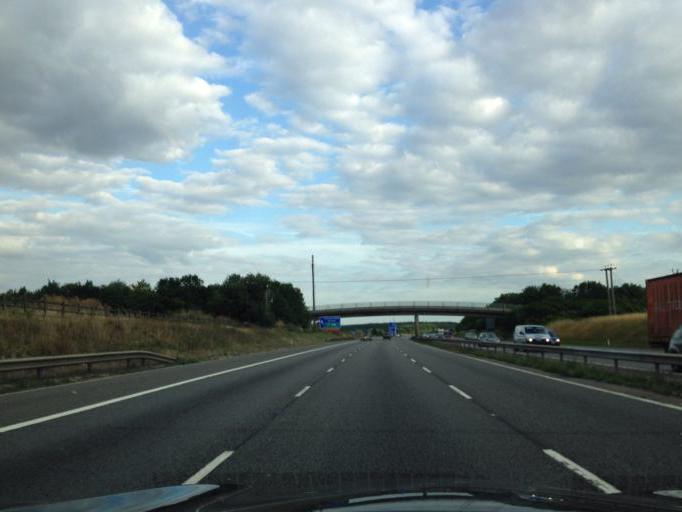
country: GB
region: England
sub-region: Oxfordshire
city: Somerton
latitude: 51.9590
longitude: -1.2163
